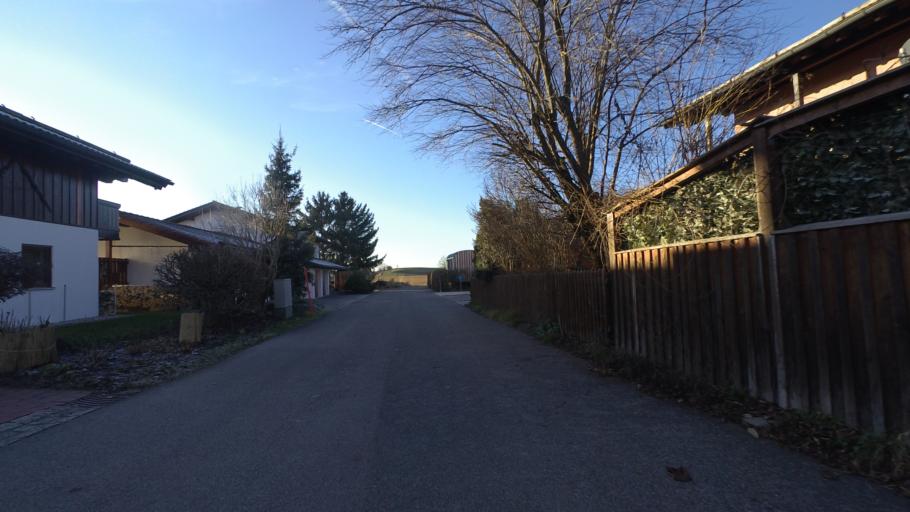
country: DE
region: Bavaria
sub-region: Upper Bavaria
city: Chieming
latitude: 47.9039
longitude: 12.5388
